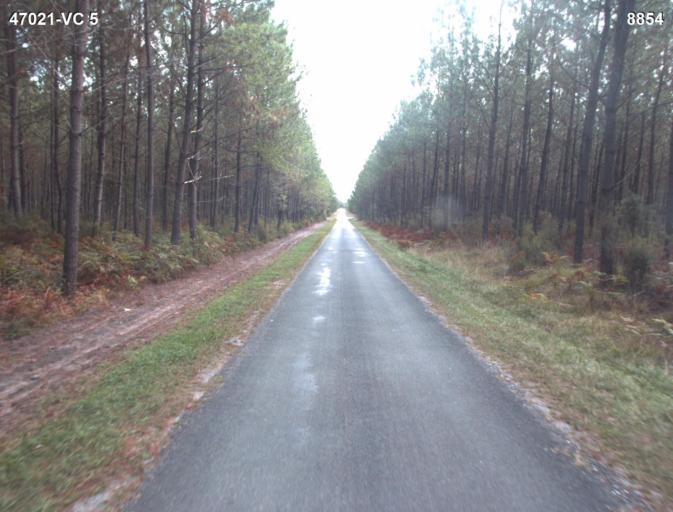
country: FR
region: Aquitaine
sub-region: Departement du Lot-et-Garonne
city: Barbaste
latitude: 44.1568
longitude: 0.1924
